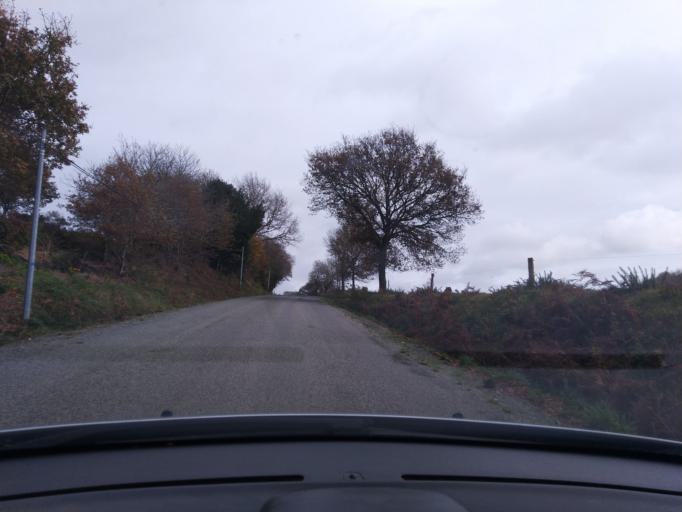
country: FR
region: Brittany
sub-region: Departement du Finistere
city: Guerlesquin
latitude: 48.5239
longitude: -3.5757
